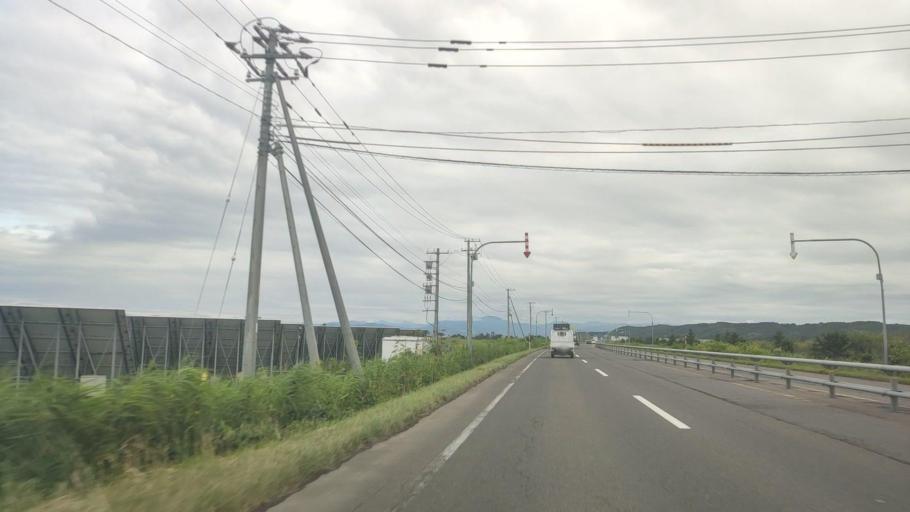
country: JP
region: Hokkaido
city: Niseko Town
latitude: 42.4027
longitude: 140.3040
